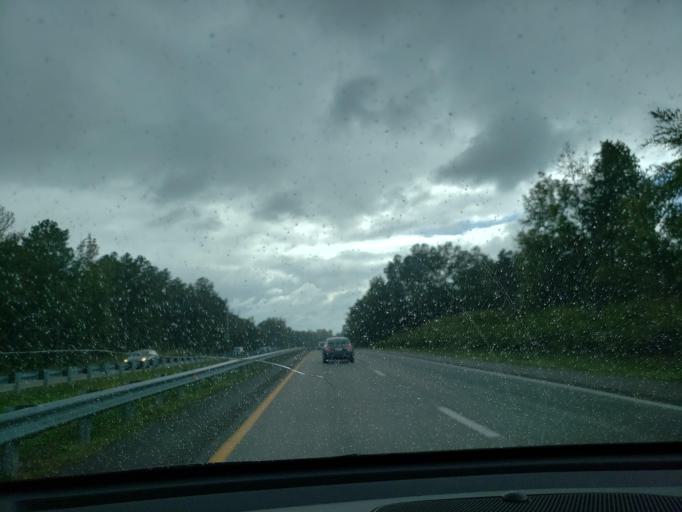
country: US
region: North Carolina
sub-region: Warren County
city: Norlina
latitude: 36.5022
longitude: -78.2152
